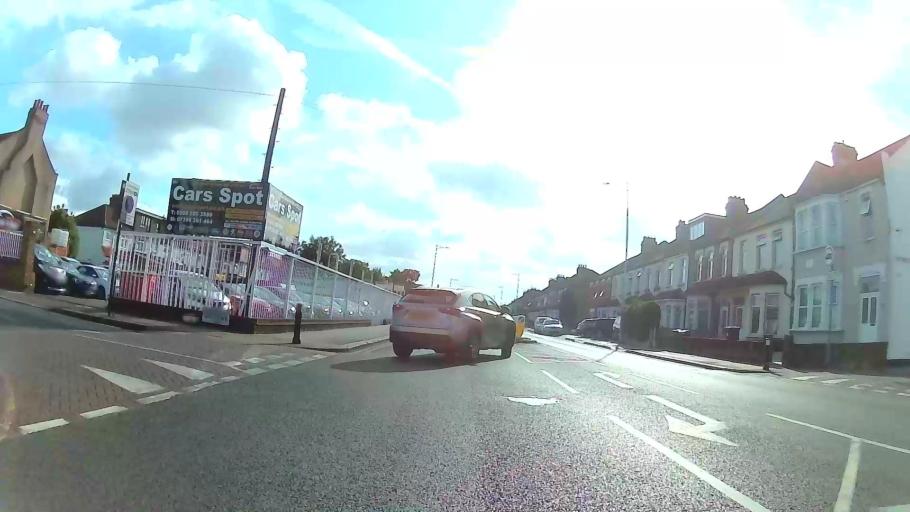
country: GB
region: England
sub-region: Greater London
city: Ilford
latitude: 51.5599
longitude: 0.0941
